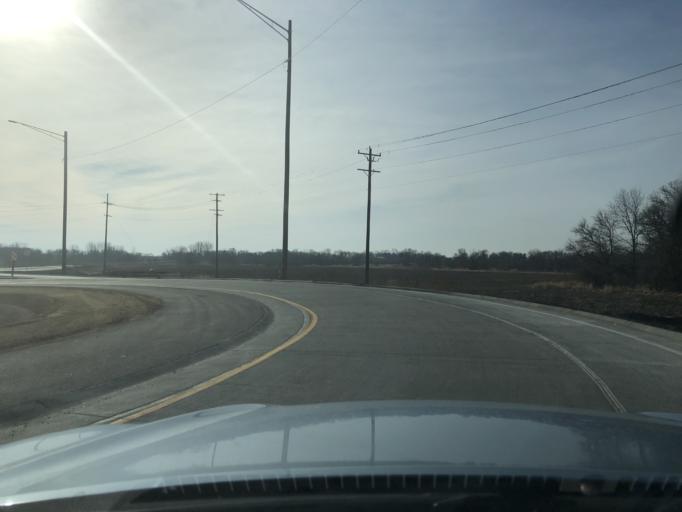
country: US
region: Illinois
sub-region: McHenry County
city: Marengo
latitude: 42.1756
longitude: -88.6181
